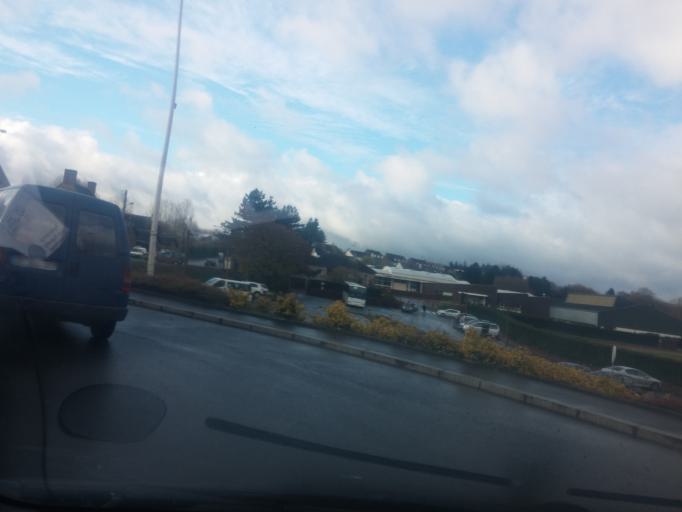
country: FR
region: Lower Normandy
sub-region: Departement du Calvados
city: Conde-sur-Noireau
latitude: 48.8498
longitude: -0.5556
